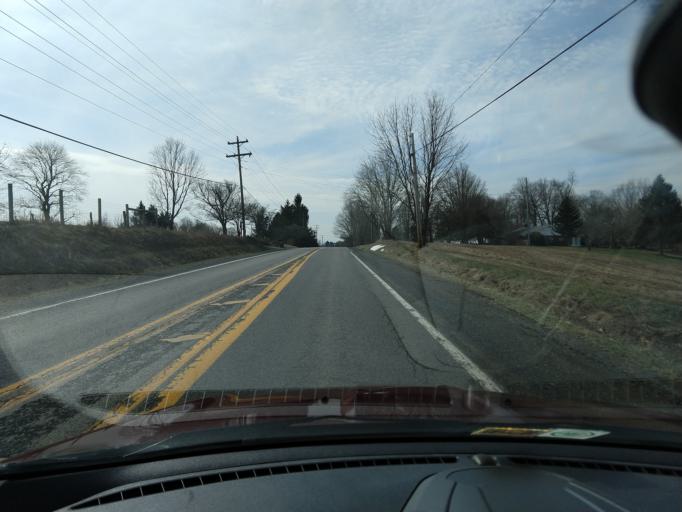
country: US
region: West Virginia
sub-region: Greenbrier County
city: Lewisburg
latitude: 37.8536
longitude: -80.4128
